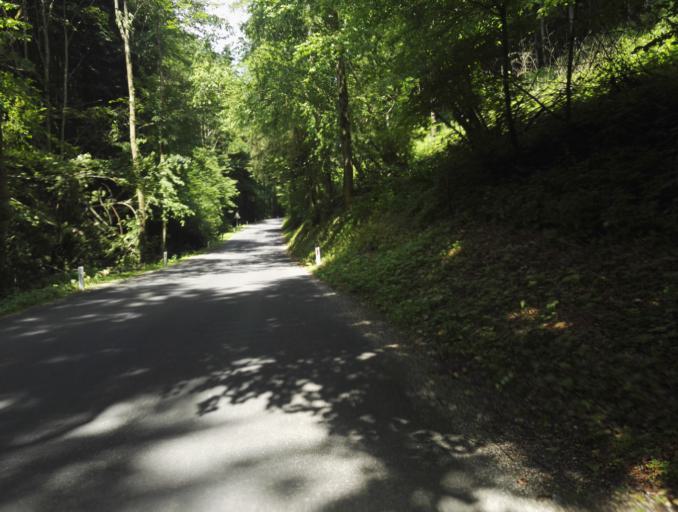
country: AT
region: Styria
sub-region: Politischer Bezirk Graz-Umgebung
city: Gratwein
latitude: 47.0941
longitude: 15.3166
